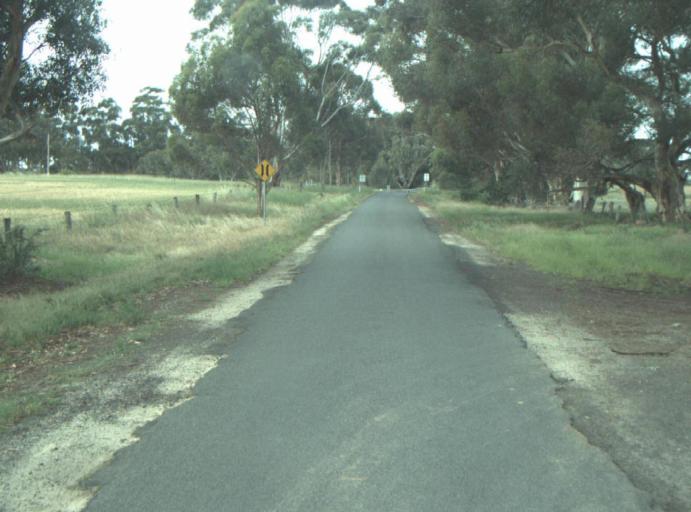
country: AU
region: Victoria
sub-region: Wyndham
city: Wyndham Vale
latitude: -37.8421
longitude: 144.3552
